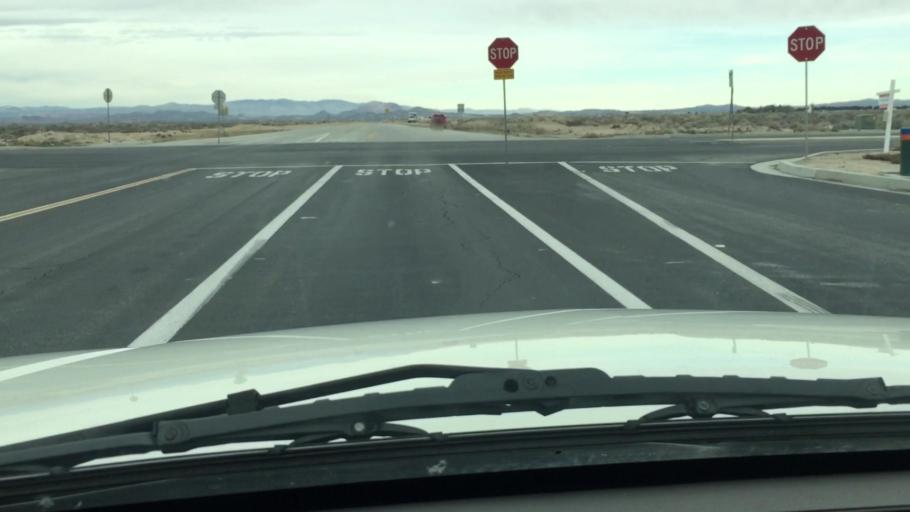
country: US
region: California
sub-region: Los Angeles County
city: Lancaster
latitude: 34.7329
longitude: -118.1840
